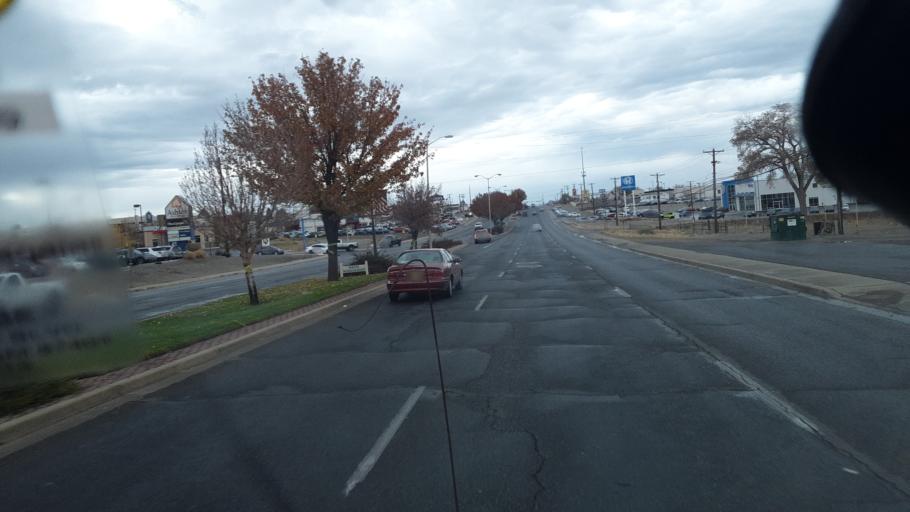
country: US
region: New Mexico
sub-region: San Juan County
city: Flora Vista
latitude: 36.7686
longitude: -108.1447
